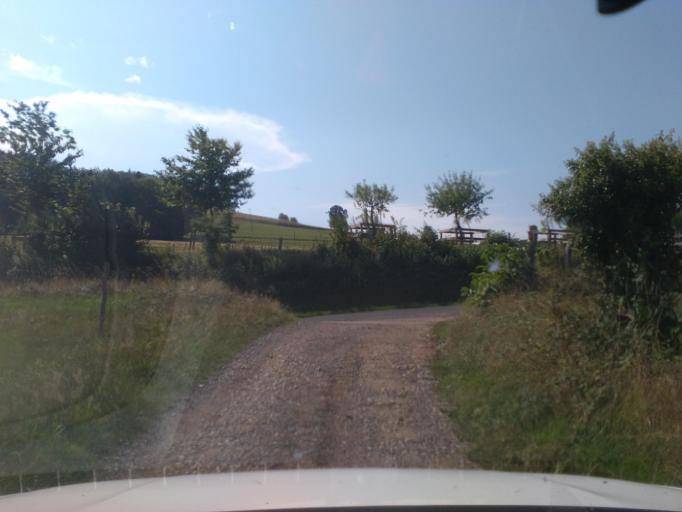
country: FR
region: Lorraine
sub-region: Departement des Vosges
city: Senones
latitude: 48.3539
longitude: 6.9997
